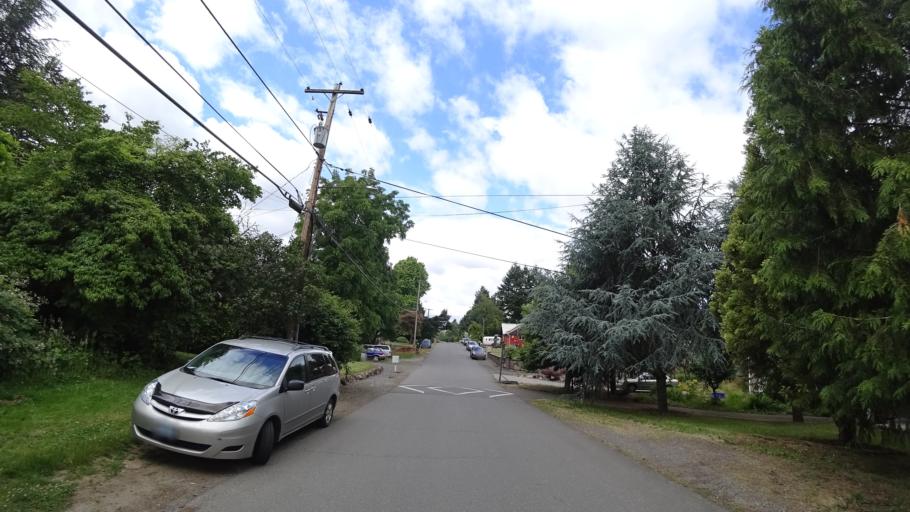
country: US
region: Oregon
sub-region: Multnomah County
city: Portland
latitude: 45.5651
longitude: -122.6125
